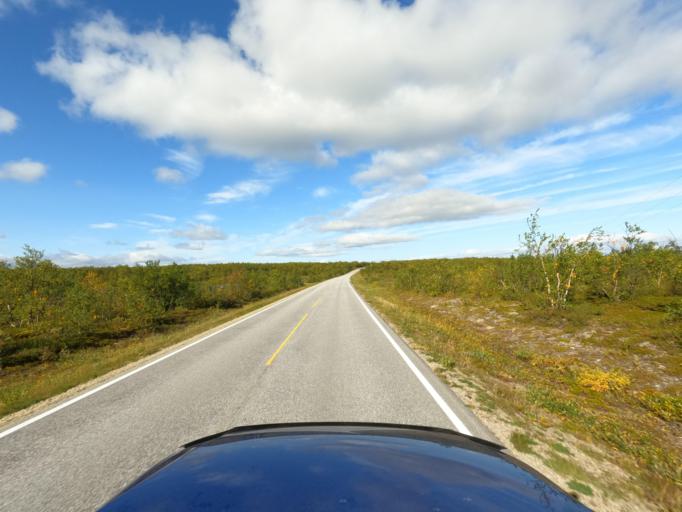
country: NO
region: Finnmark Fylke
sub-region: Karasjok
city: Karasjohka
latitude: 69.6121
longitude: 25.3063
